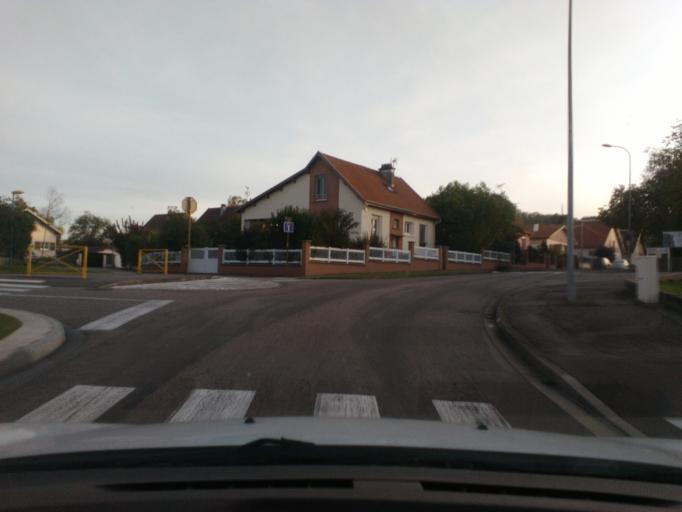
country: FR
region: Lorraine
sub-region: Departement des Vosges
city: Charmes
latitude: 48.3724
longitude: 6.2865
